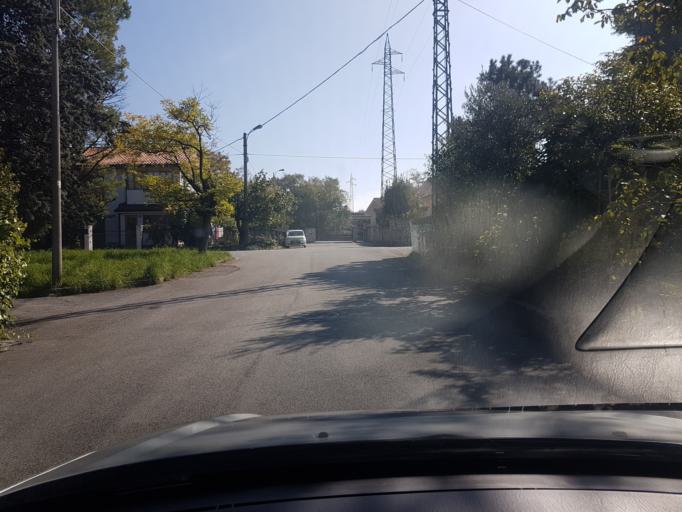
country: IT
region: Friuli Venezia Giulia
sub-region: Provincia di Trieste
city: Sistiana-Visogliano
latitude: 45.7653
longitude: 13.6429
